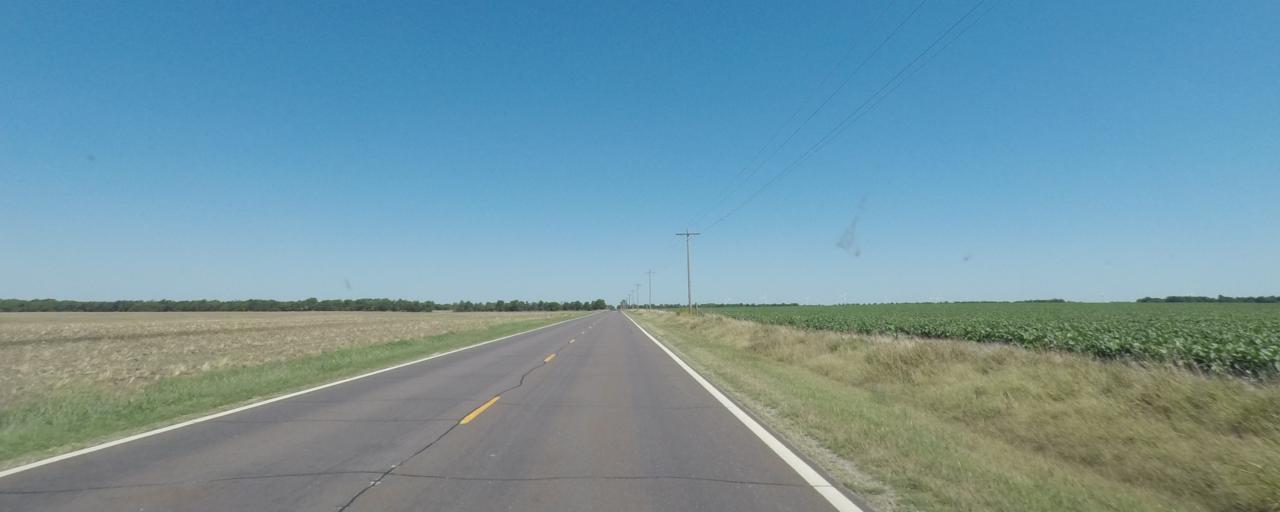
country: US
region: Kansas
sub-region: Sumner County
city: Wellington
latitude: 37.0900
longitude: -97.4015
